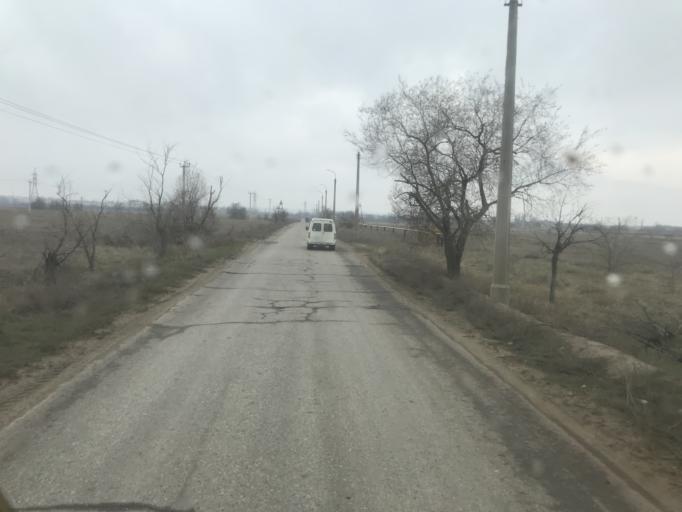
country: RU
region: Volgograd
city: Krasnoslobodsk
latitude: 48.5343
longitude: 44.6023
